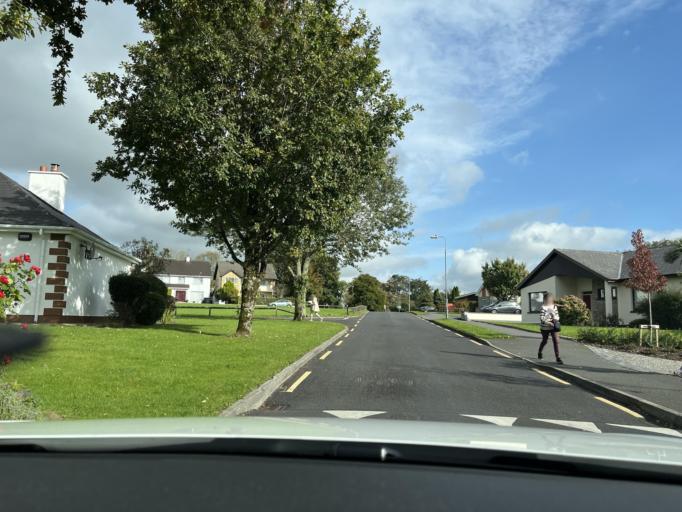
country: IE
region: Connaught
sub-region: County Leitrim
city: Carrick-on-Shannon
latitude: 53.9442
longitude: -8.0896
